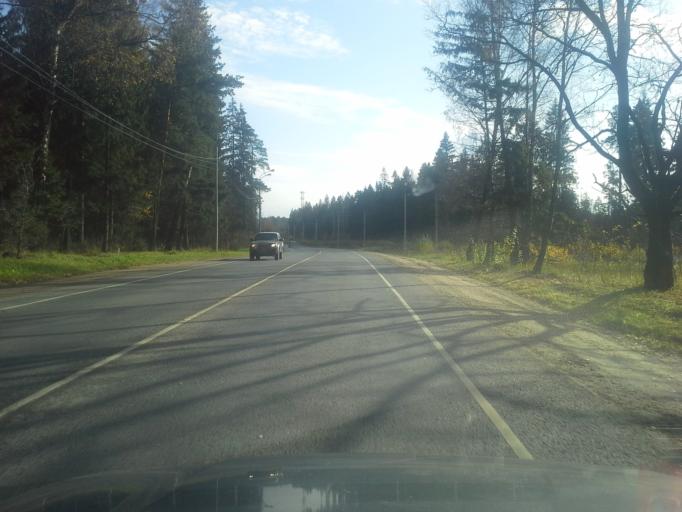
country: RU
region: Moskovskaya
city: Bol'shiye Vyazemy
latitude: 55.6741
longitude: 36.9368
